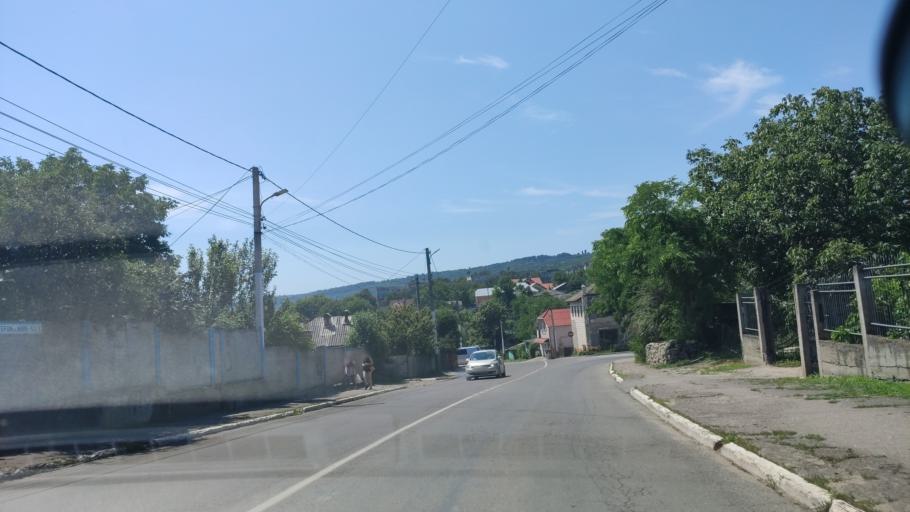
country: MD
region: Raionul Soroca
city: Soroca
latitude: 48.1646
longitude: 28.3044
